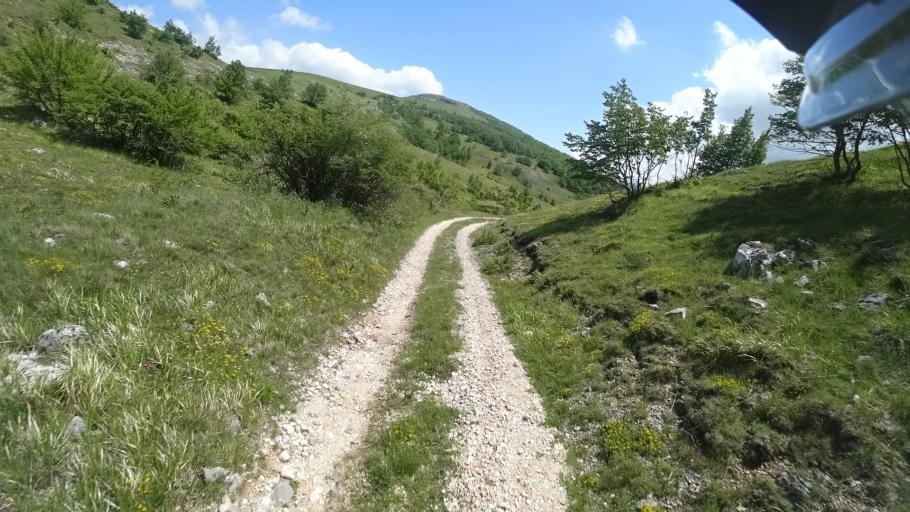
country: HR
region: Zadarska
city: Gracac
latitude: 44.3694
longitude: 15.9534
